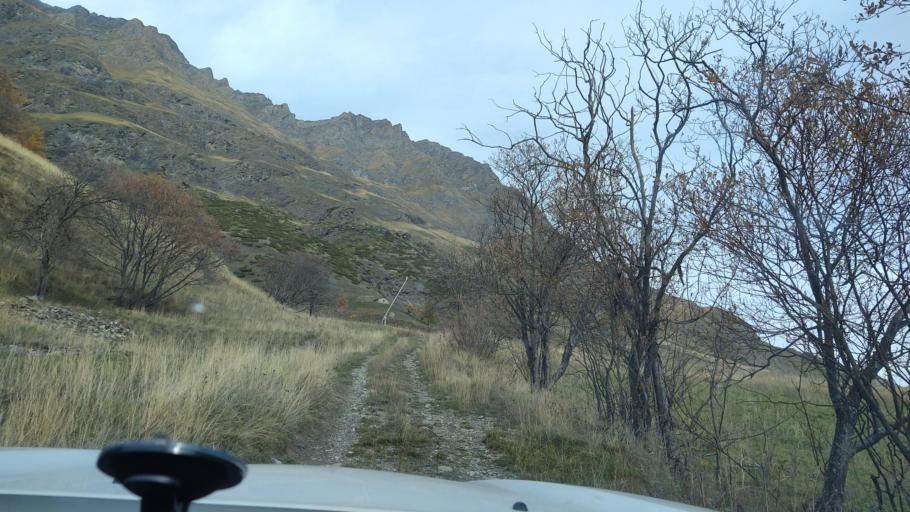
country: IT
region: Piedmont
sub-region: Provincia di Torino
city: Moncenisio
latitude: 45.3244
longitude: 6.9880
